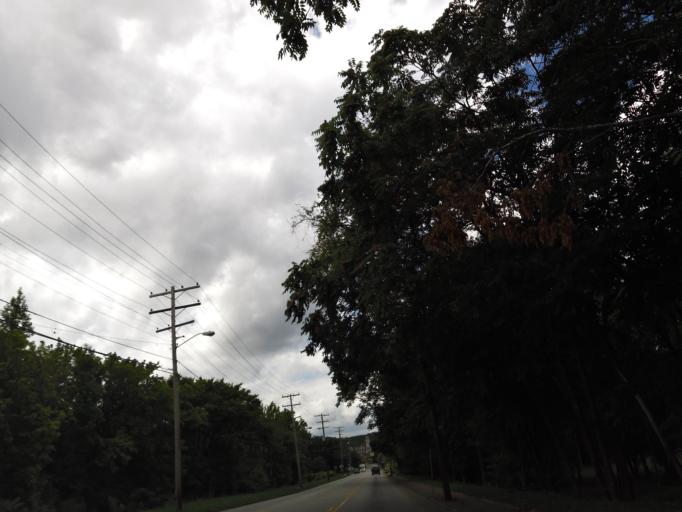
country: US
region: Tennessee
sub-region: Hamilton County
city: Chattanooga
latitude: 35.0112
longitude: -85.3164
